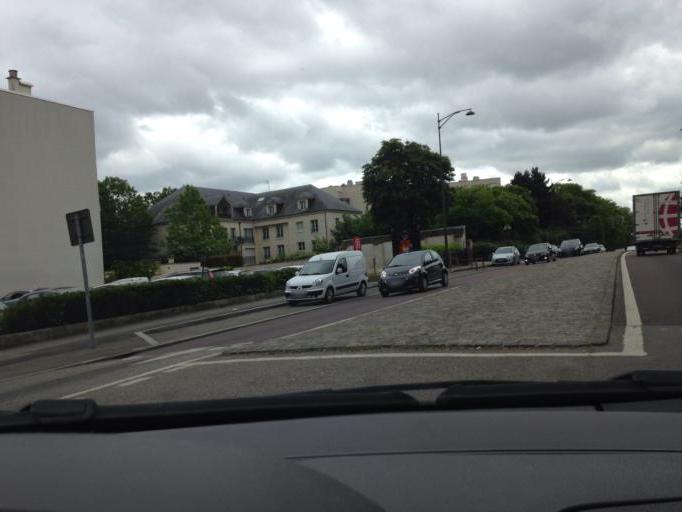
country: FR
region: Ile-de-France
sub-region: Departement des Yvelines
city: Viroflay
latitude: 48.8145
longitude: 2.1507
